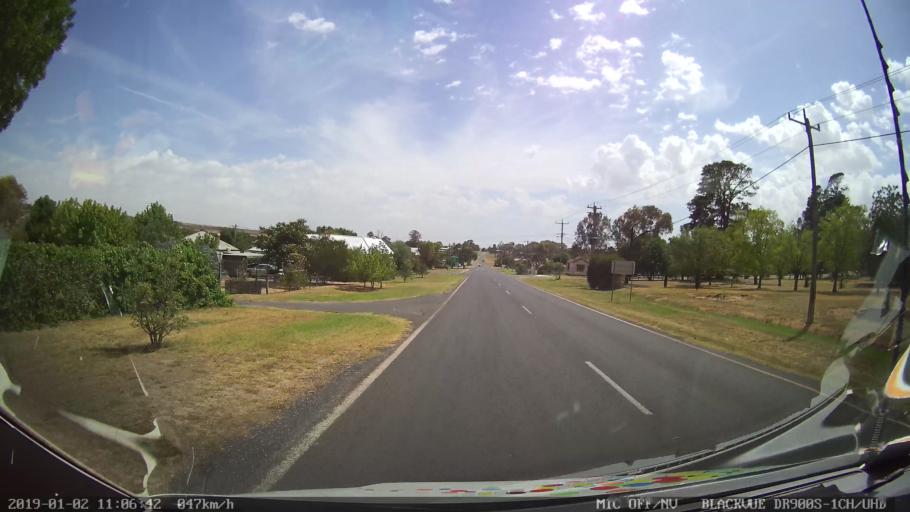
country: AU
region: New South Wales
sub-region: Young
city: Young
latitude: -34.5536
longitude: 148.3572
